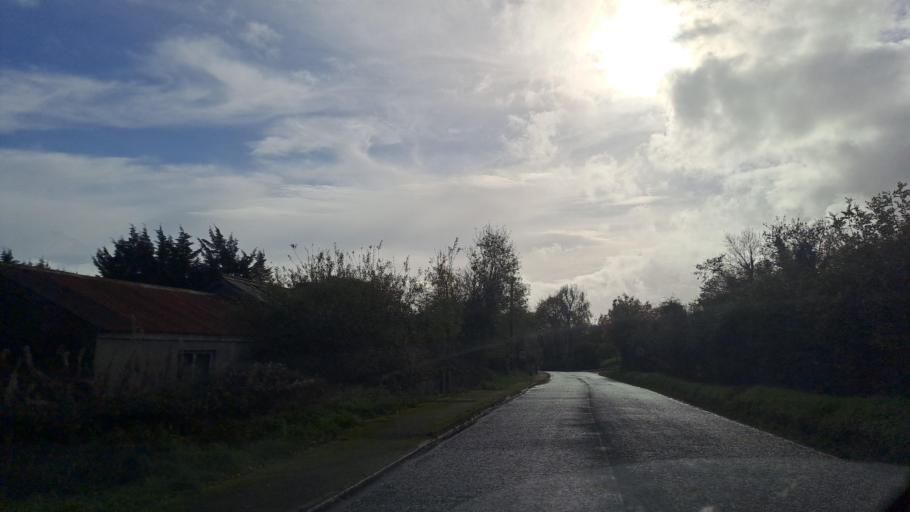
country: IE
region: Leinster
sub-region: Lu
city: Ardee
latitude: 53.8548
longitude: -6.6575
